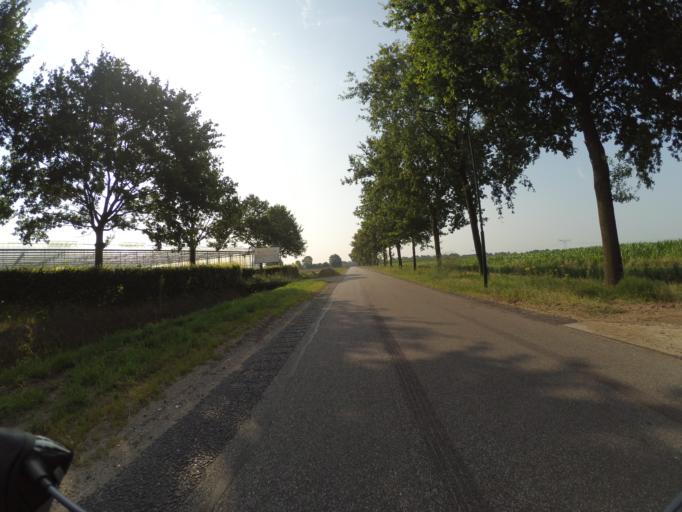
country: NL
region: North Brabant
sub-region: Gemeente Dongen
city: Dongen
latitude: 51.6337
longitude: 4.9656
